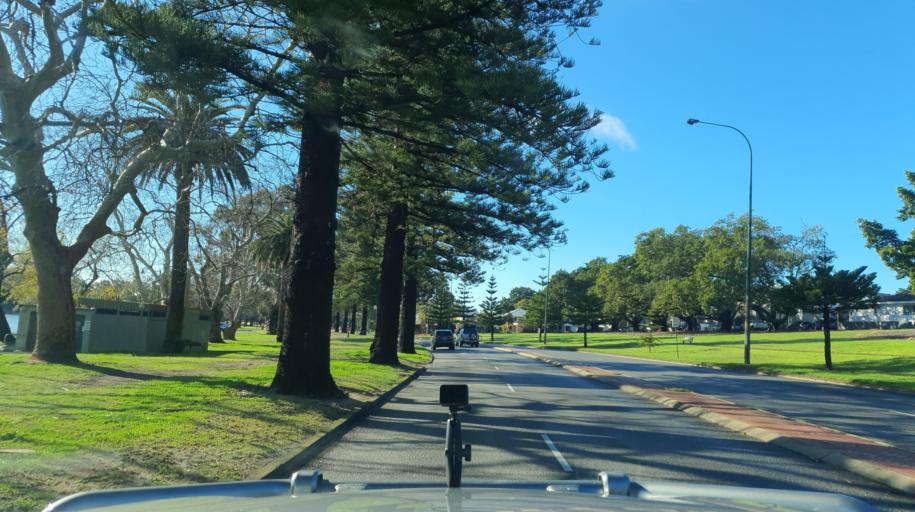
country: AU
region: Western Australia
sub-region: Cambridge
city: West Leederville
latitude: -31.9336
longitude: 115.8301
